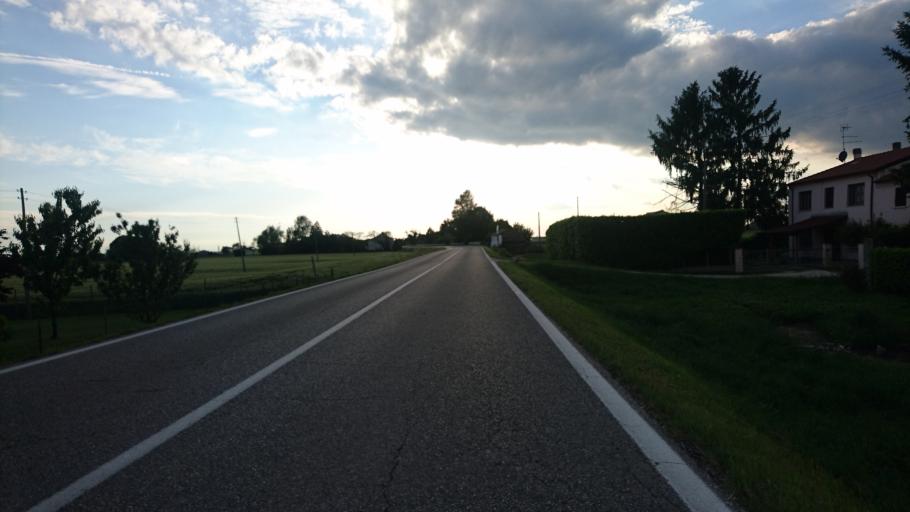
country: IT
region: Veneto
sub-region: Provincia di Rovigo
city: Ceneselli
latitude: 45.0212
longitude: 11.3536
